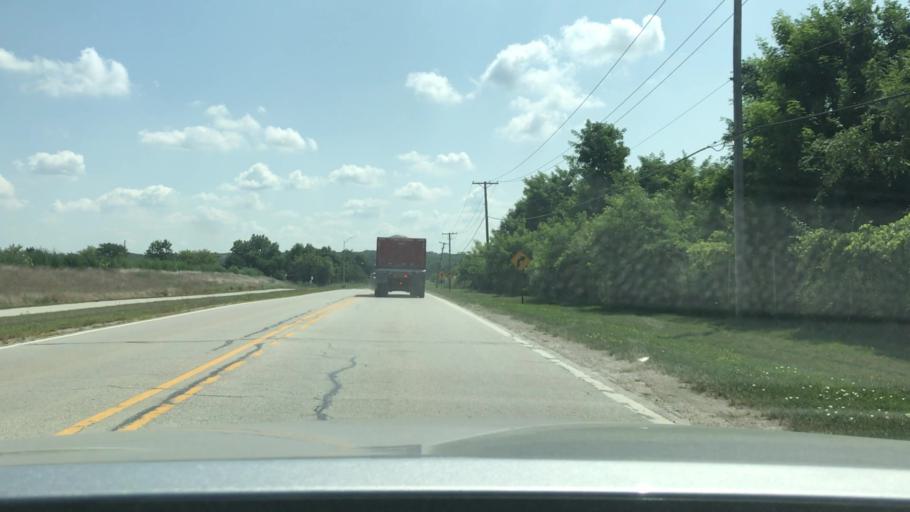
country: US
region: Illinois
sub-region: Will County
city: Bolingbrook
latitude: 41.7200
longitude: -88.0812
